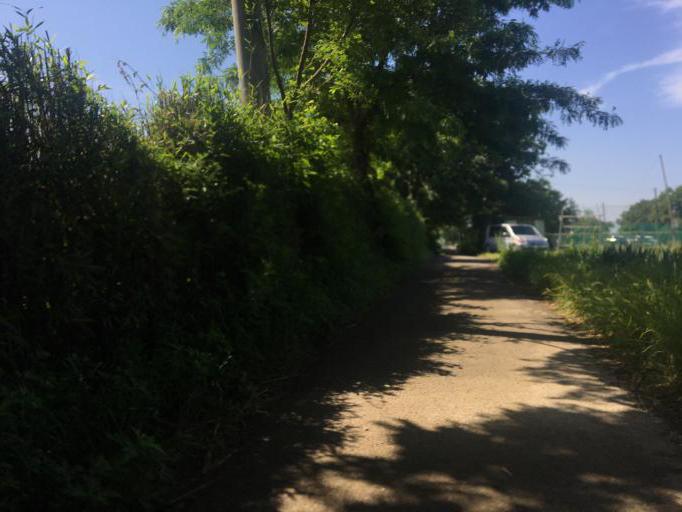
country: JP
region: Saitama
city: Shiki
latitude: 35.8611
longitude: 139.5897
